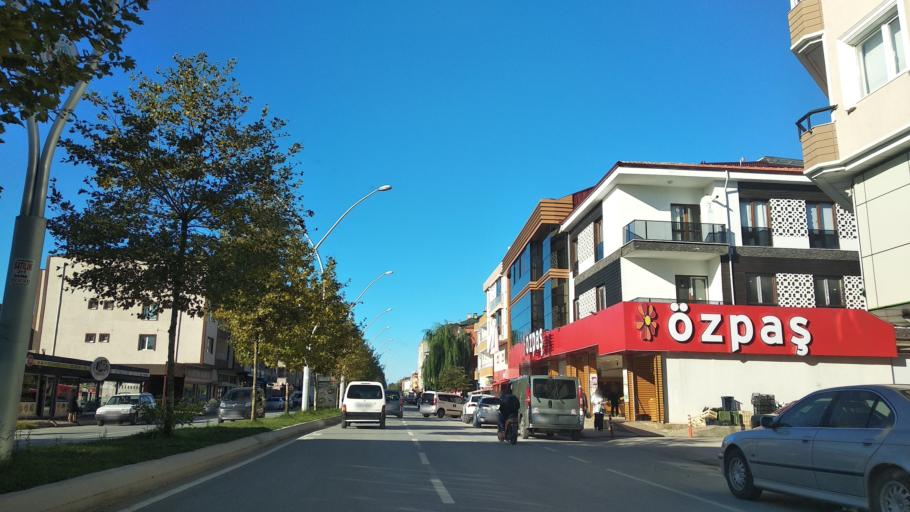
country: TR
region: Sakarya
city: Karasu
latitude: 41.0997
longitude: 30.6926
